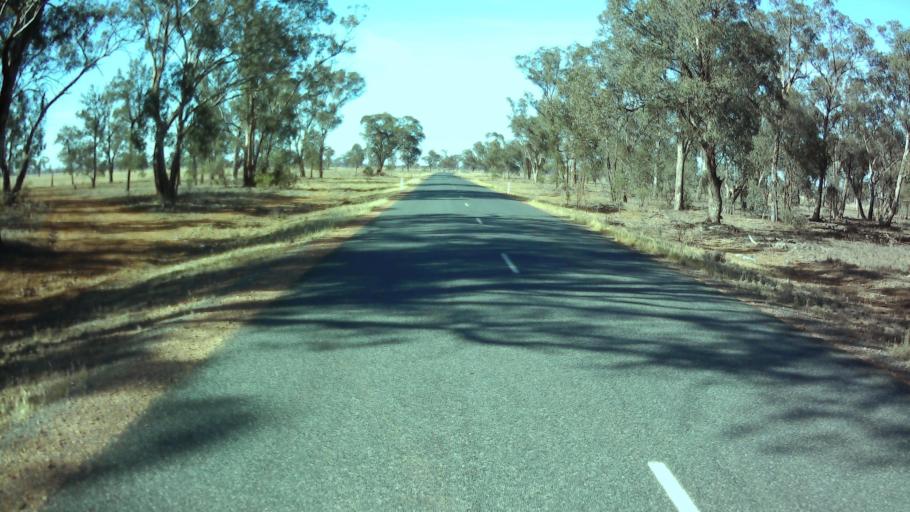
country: AU
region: New South Wales
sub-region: Weddin
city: Grenfell
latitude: -34.0668
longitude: 147.9064
